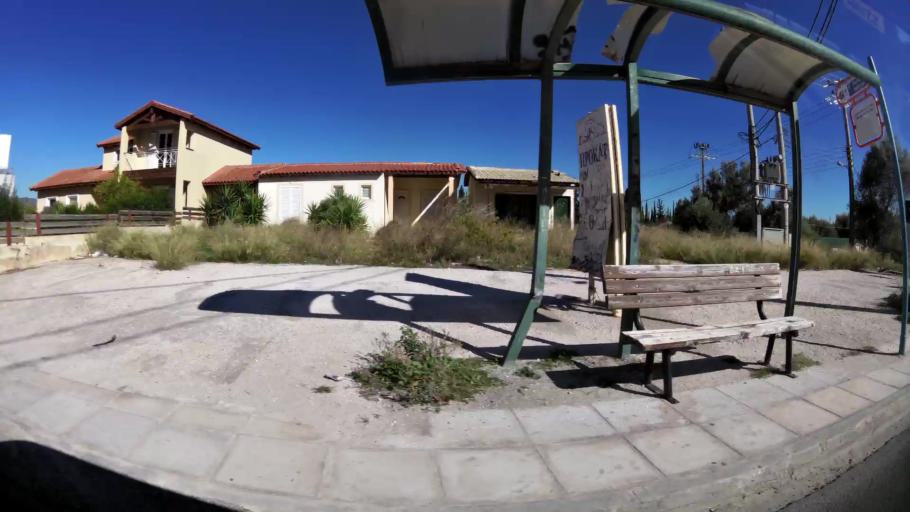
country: GR
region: Attica
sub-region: Nomarchia Anatolikis Attikis
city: Leondarion
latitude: 37.9770
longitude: 23.8534
